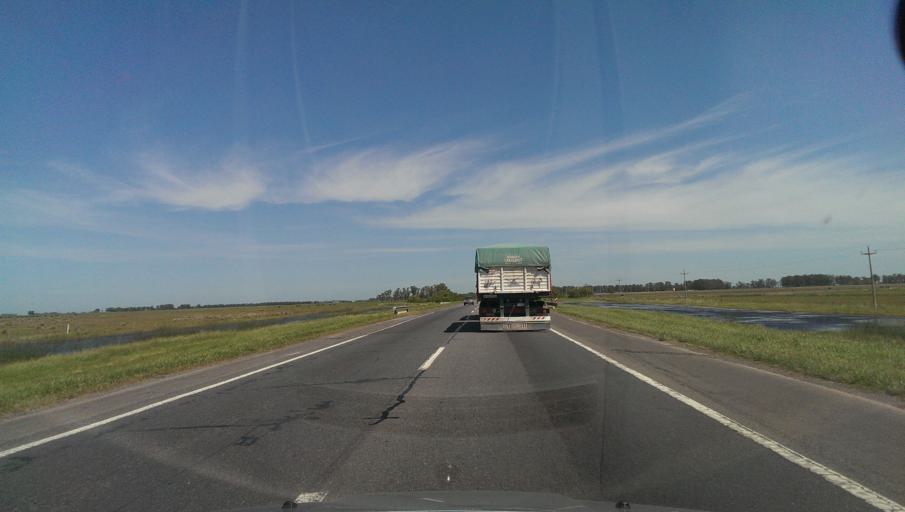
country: AR
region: Buenos Aires
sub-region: Partido de Las Flores
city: Las Flores
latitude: -35.7550
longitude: -58.9271
